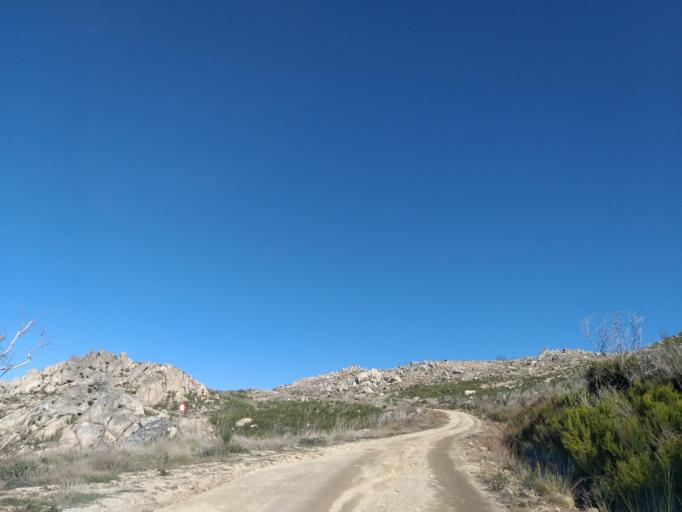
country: PT
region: Guarda
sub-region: Manteigas
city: Manteigas
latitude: 40.4847
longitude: -7.5082
